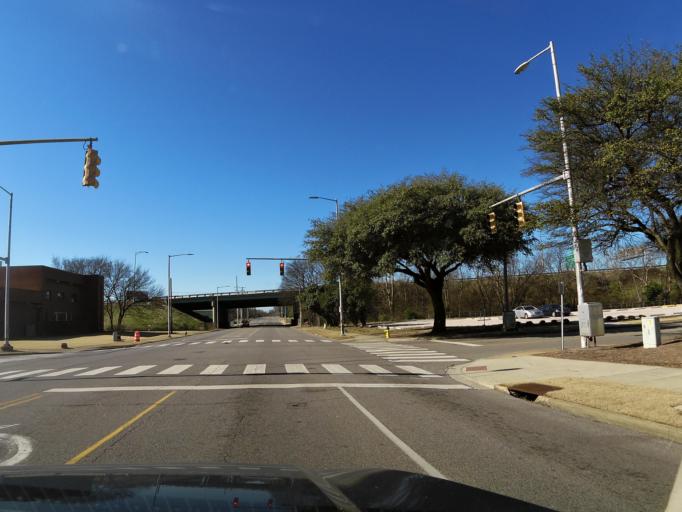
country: US
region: Alabama
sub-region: Jefferson County
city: Birmingham
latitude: 33.5013
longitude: -86.8127
